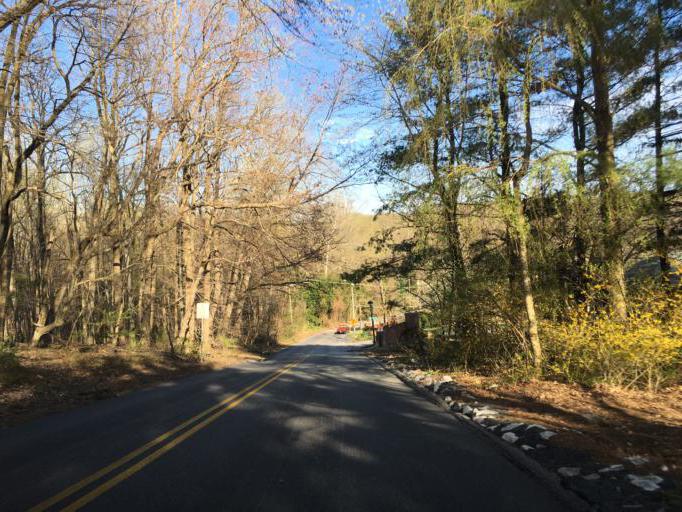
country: US
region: Maryland
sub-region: Baltimore County
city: Cockeysville
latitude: 39.4751
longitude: -76.6137
